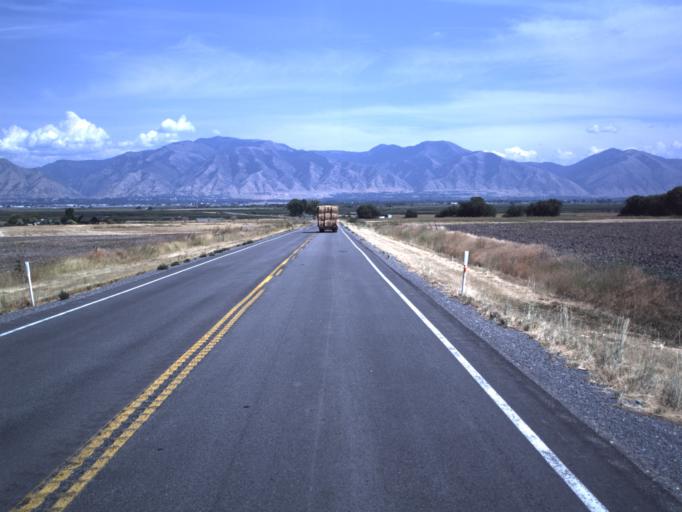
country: US
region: Utah
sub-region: Cache County
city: Mendon
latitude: 41.7494
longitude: -111.9737
